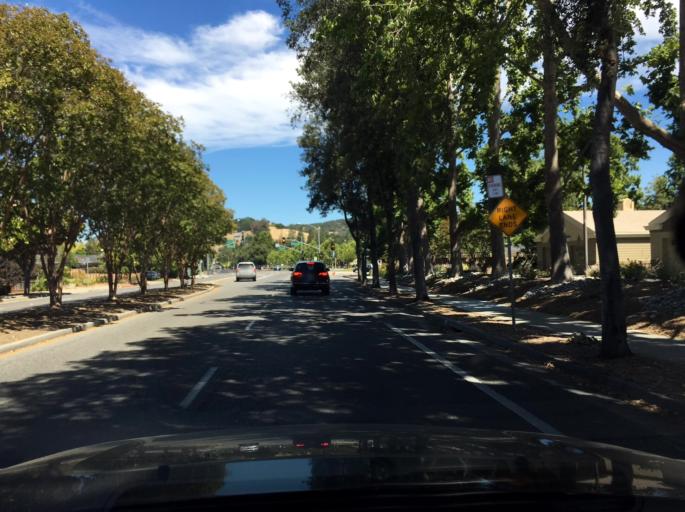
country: US
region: California
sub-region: Santa Clara County
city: Los Gatos
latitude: 37.2350
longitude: -121.9589
